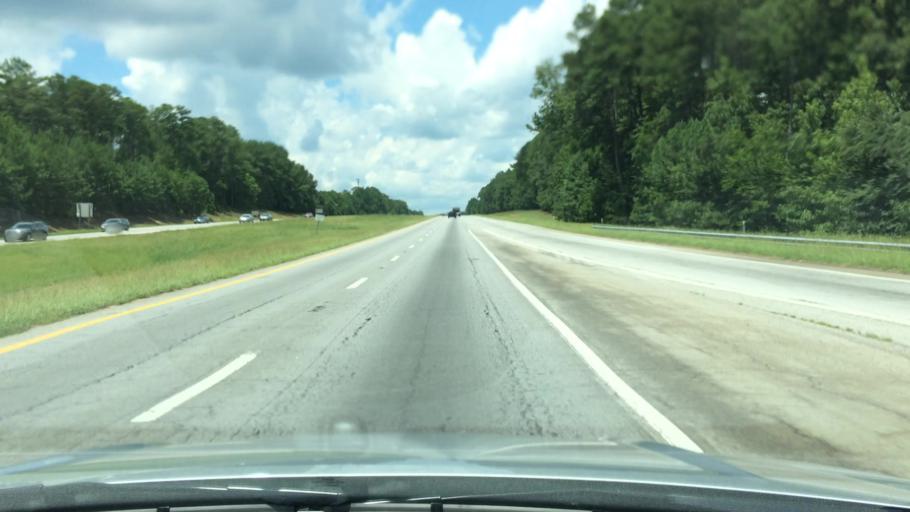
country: US
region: South Carolina
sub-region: Laurens County
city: Joanna
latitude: 34.4150
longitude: -81.7082
